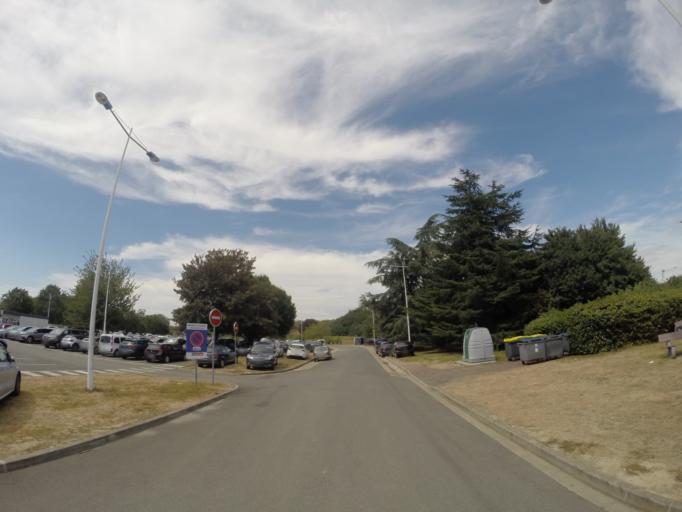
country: FR
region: Centre
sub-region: Departement d'Indre-et-Loire
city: Parcay-Meslay
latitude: 47.4261
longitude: 0.7187
